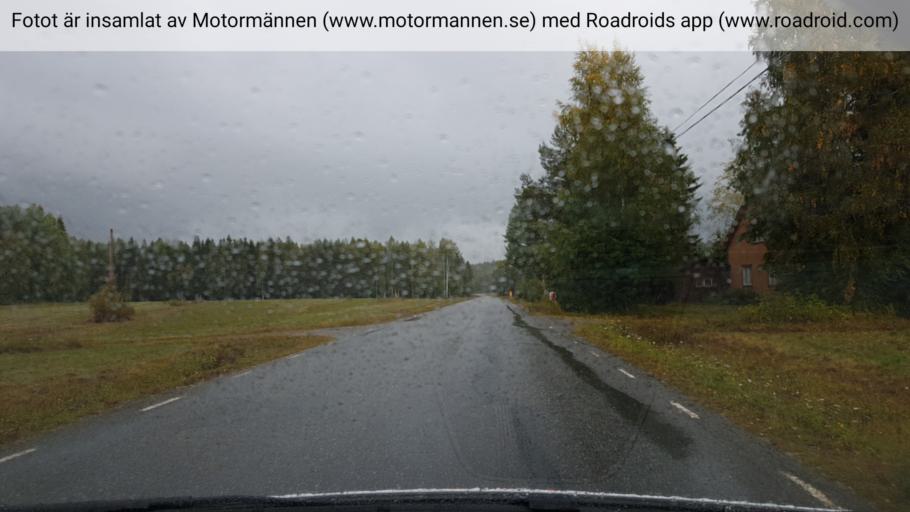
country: SE
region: Vaesterbotten
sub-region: Vannas Kommun
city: Vannasby
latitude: 63.9877
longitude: 19.9019
